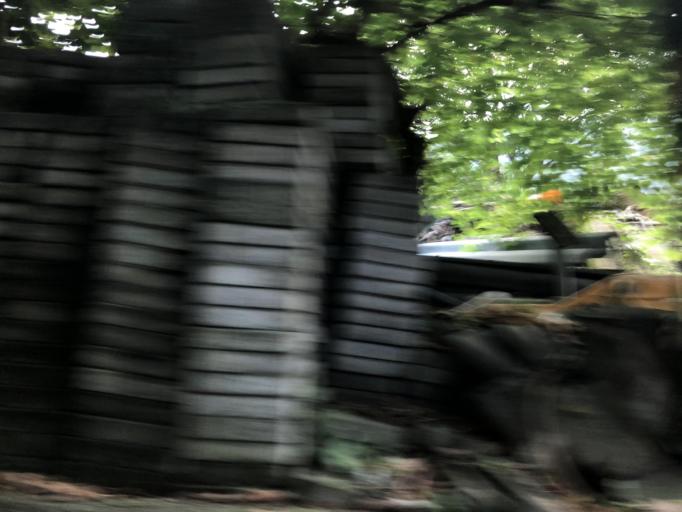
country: TW
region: Taiwan
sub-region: Keelung
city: Keelung
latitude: 25.1911
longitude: 121.6435
